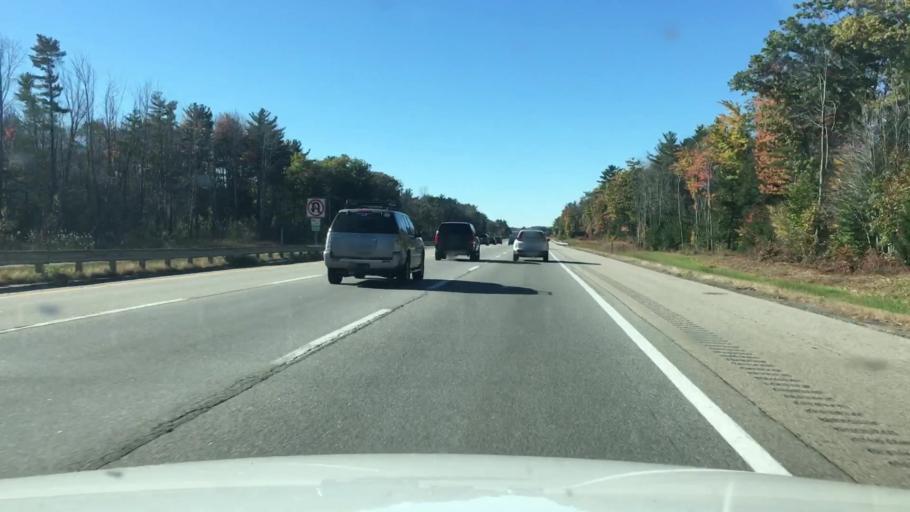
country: US
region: Maine
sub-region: York County
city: Saco
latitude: 43.5381
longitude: -70.4419
